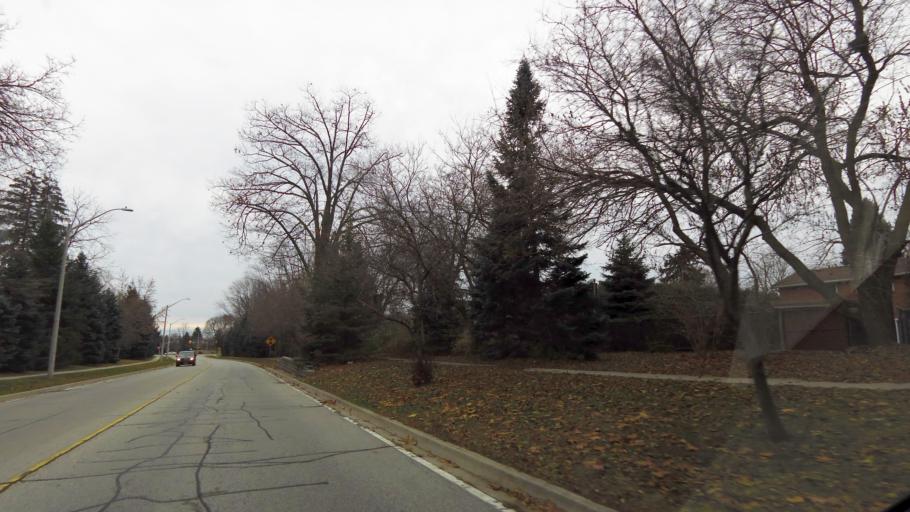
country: CA
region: Ontario
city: Oakville
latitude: 43.4775
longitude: -79.6377
